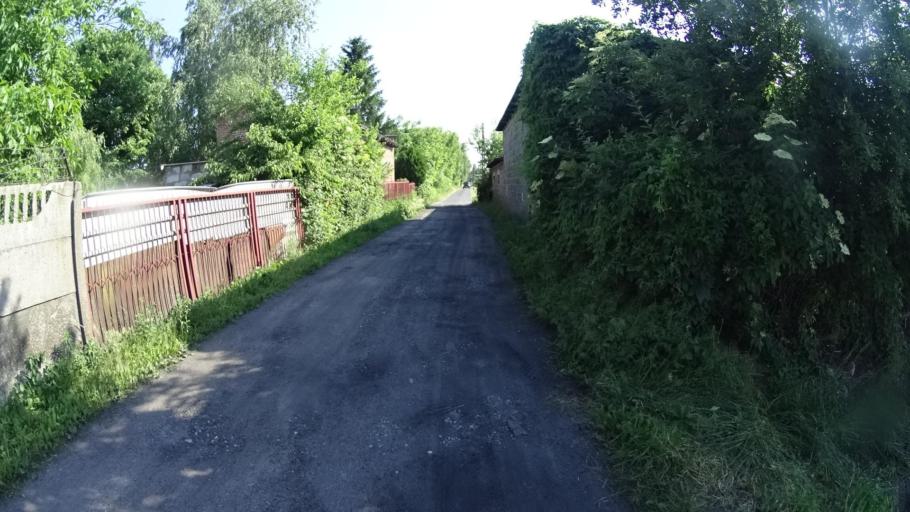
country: PL
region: Masovian Voivodeship
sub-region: Powiat warszawski zachodni
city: Ozarow Mazowiecki
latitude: 52.1920
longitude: 20.7557
